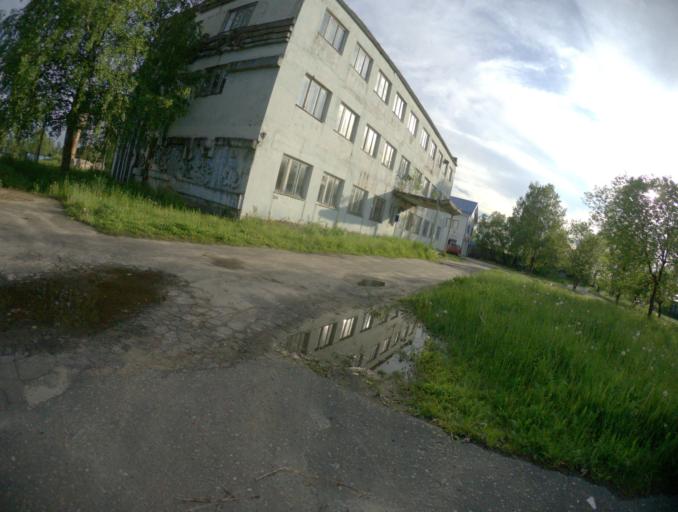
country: RU
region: Vladimir
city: Zolotkovo
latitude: 55.5097
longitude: 40.9603
